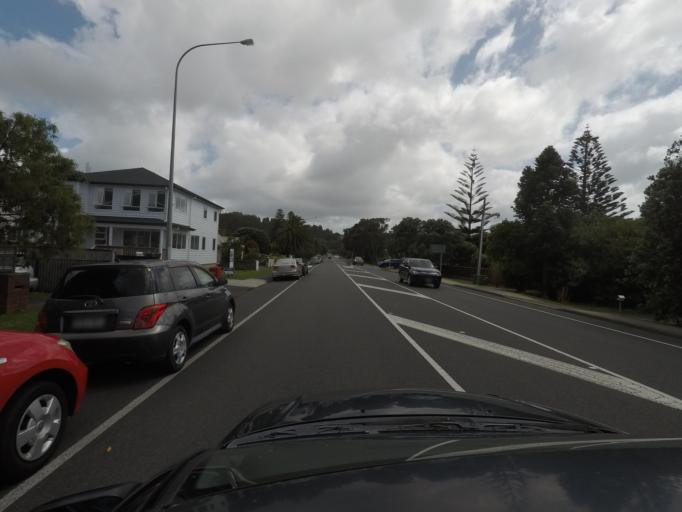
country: NZ
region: Auckland
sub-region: Auckland
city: Rothesay Bay
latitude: -36.5790
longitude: 174.6922
